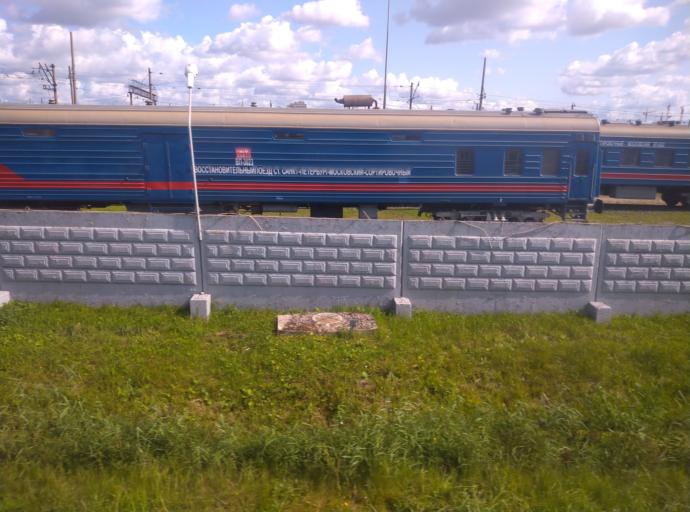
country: RU
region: St.-Petersburg
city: Kupchino
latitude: 59.8891
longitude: 30.3955
